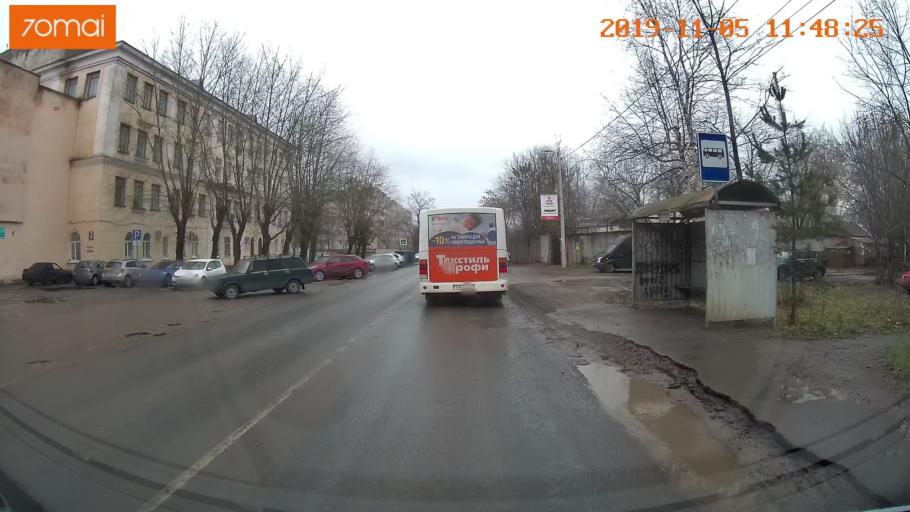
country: RU
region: Ivanovo
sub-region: Gorod Ivanovo
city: Ivanovo
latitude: 57.0086
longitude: 40.9973
